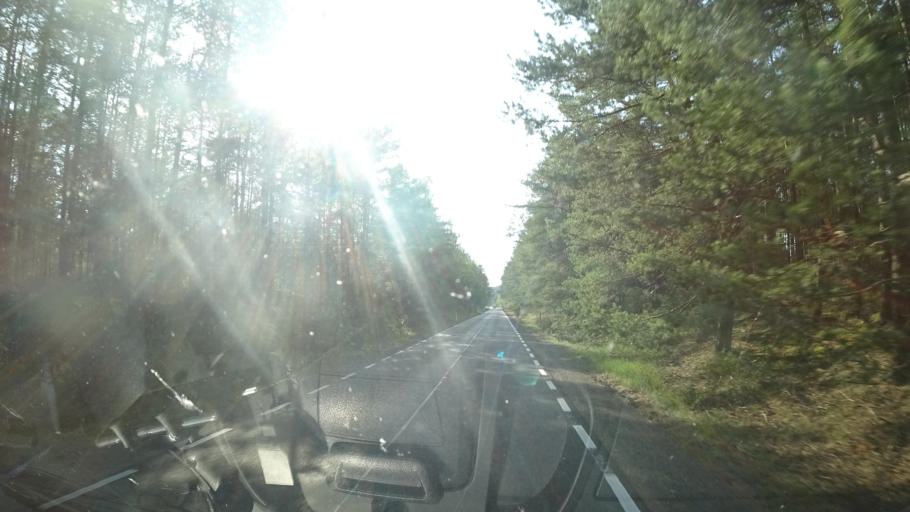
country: PL
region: Pomeranian Voivodeship
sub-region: Powiat chojnicki
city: Chojnice
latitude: 53.8619
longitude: 17.5233
